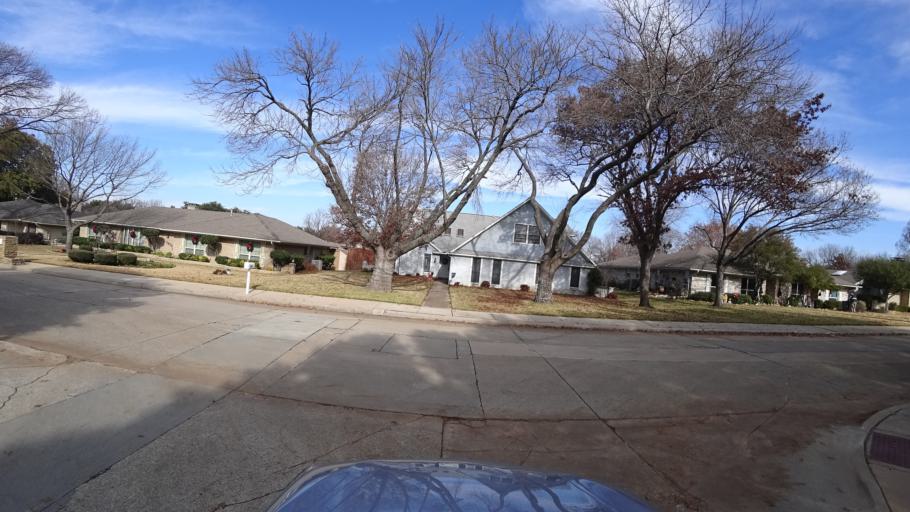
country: US
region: Texas
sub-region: Denton County
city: Lewisville
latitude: 33.0518
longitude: -97.0321
